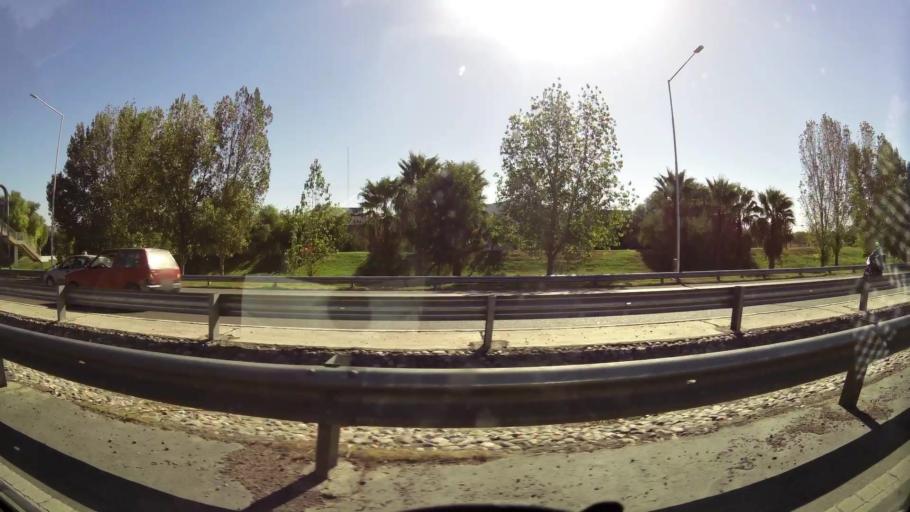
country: AR
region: San Juan
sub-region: Departamento de Santa Lucia
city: Santa Lucia
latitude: -31.5248
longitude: -68.5030
